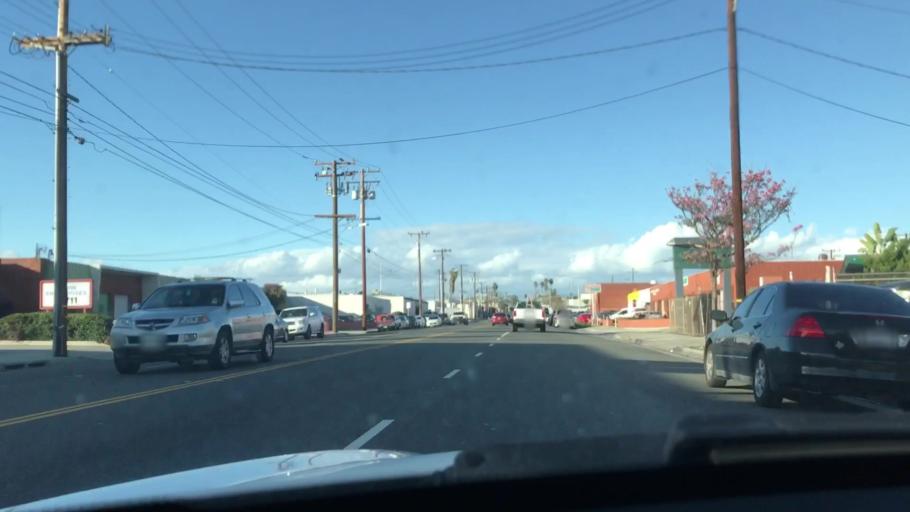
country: US
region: California
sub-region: Los Angeles County
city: West Athens
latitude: 33.9069
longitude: -118.3004
